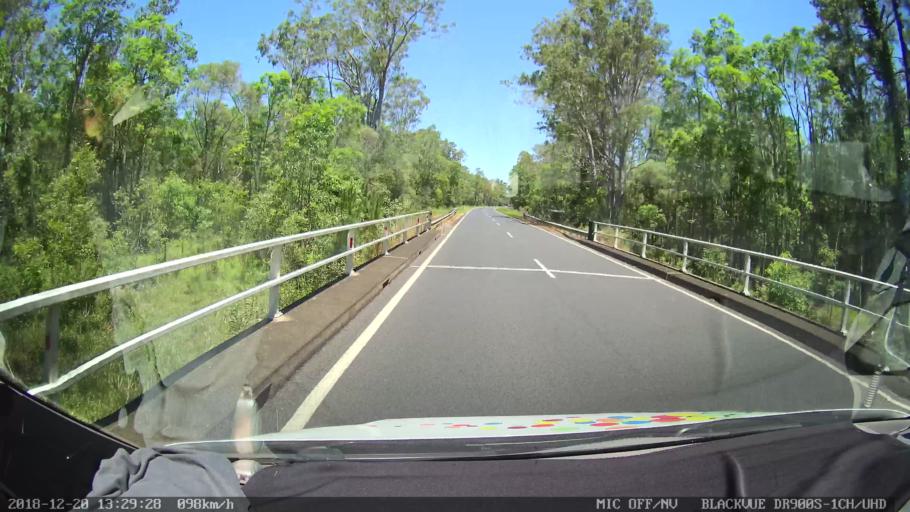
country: AU
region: New South Wales
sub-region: Clarence Valley
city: Gordon
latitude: -29.1894
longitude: 152.9897
